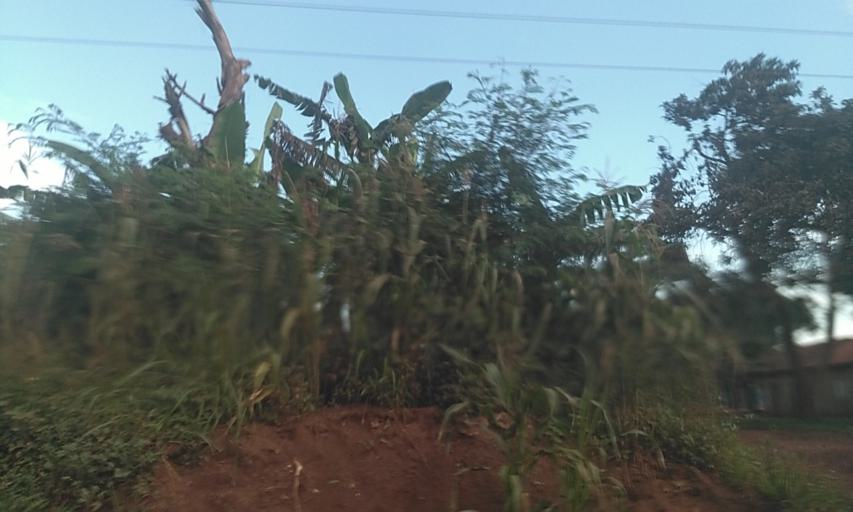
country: UG
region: Central Region
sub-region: Wakiso District
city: Kajansi
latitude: 0.2613
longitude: 32.5103
